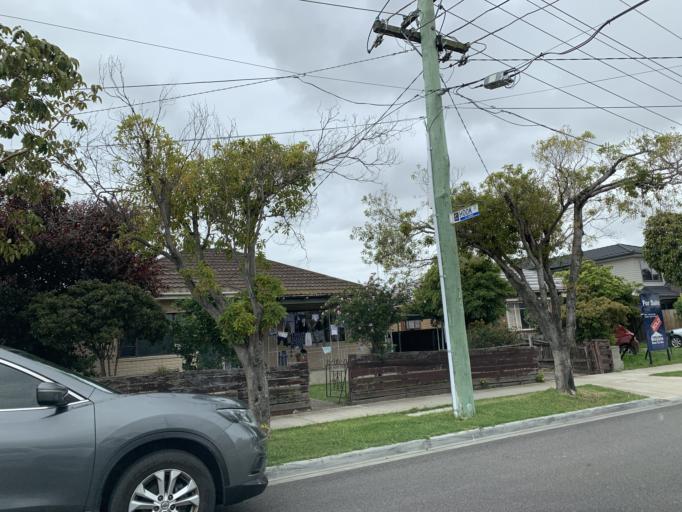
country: AU
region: Victoria
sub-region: Brimbank
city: St Albans
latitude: -37.7451
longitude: 144.7924
